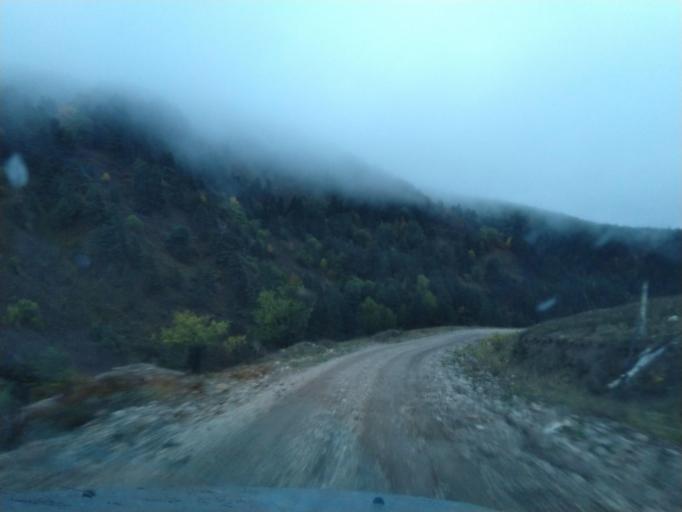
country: RU
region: North Ossetia
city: Tarskoye
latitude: 42.8261
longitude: 44.9760
